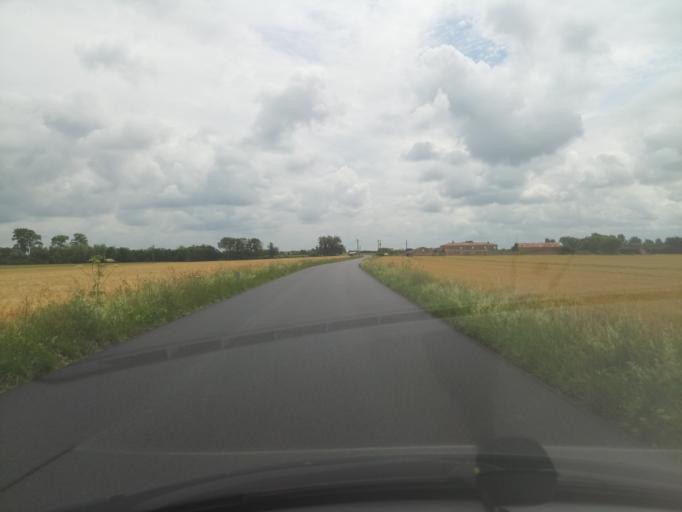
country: FR
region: Poitou-Charentes
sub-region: Departement de la Charente-Maritime
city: Saint-Jean-de-Liversay
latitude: 46.2717
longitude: -0.8980
